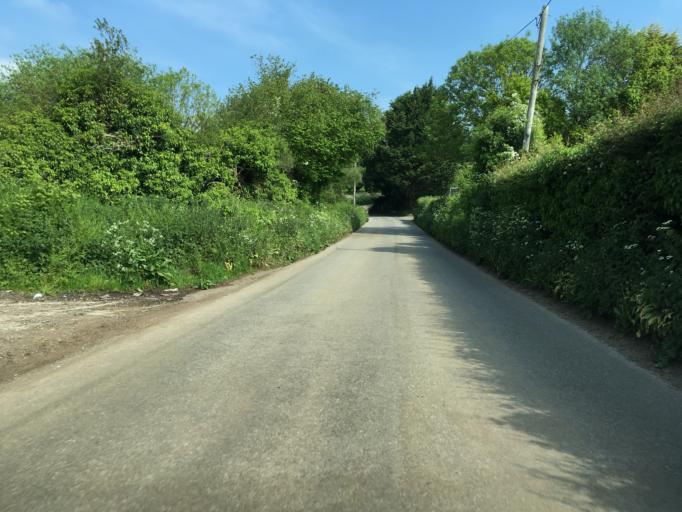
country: GB
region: England
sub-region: North Somerset
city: Butcombe
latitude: 51.3939
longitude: -2.7109
